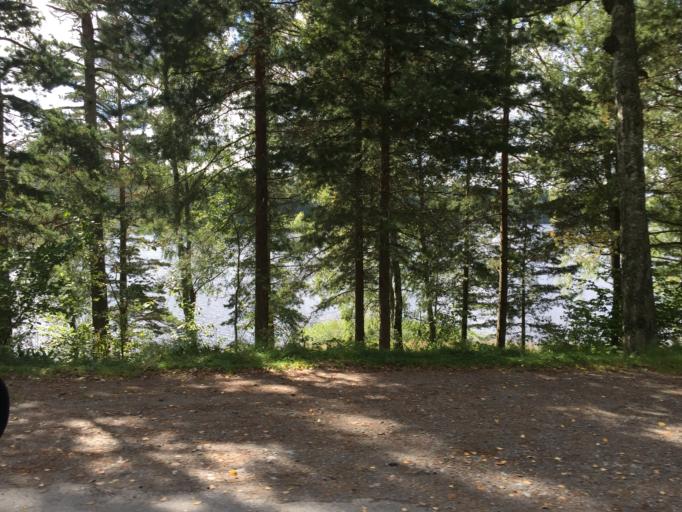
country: SE
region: Stockholm
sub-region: Botkyrka Kommun
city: Tullinge
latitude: 59.1616
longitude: 17.8847
